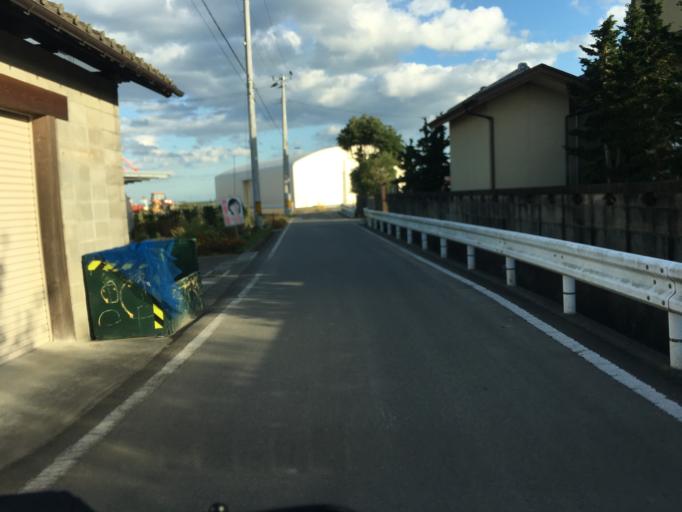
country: JP
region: Miyagi
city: Marumori
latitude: 37.7889
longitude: 140.9543
